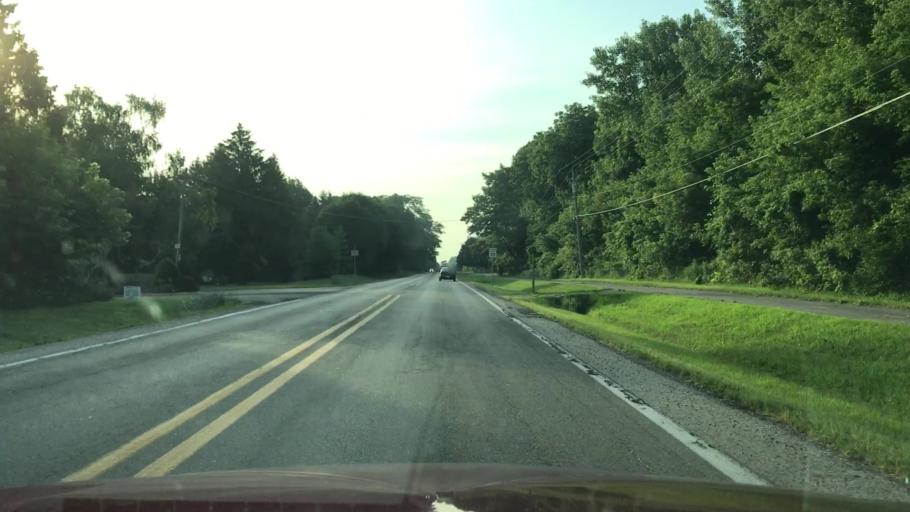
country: US
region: Illinois
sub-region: Winnebago County
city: Cherry Valley
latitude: 42.2454
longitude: -89.0076
